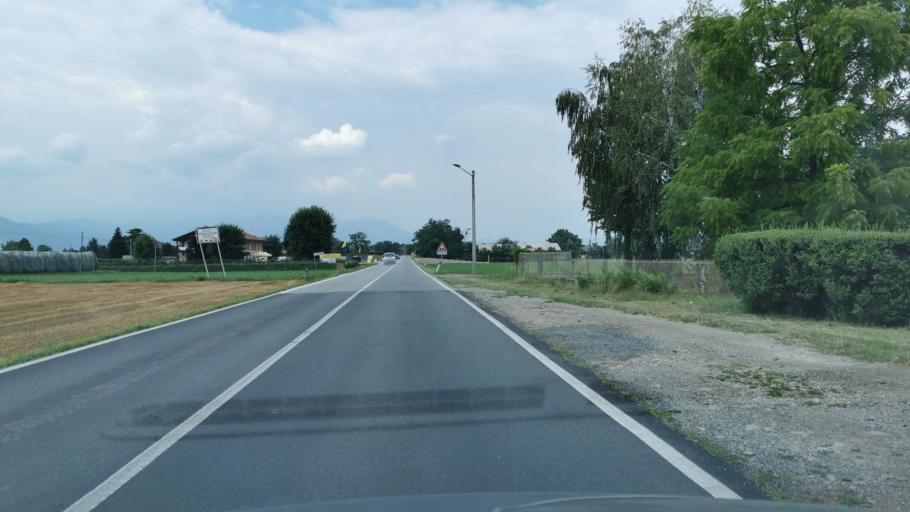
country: IT
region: Piedmont
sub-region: Provincia di Torino
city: Garzigliana
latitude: 44.8192
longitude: 7.3708
